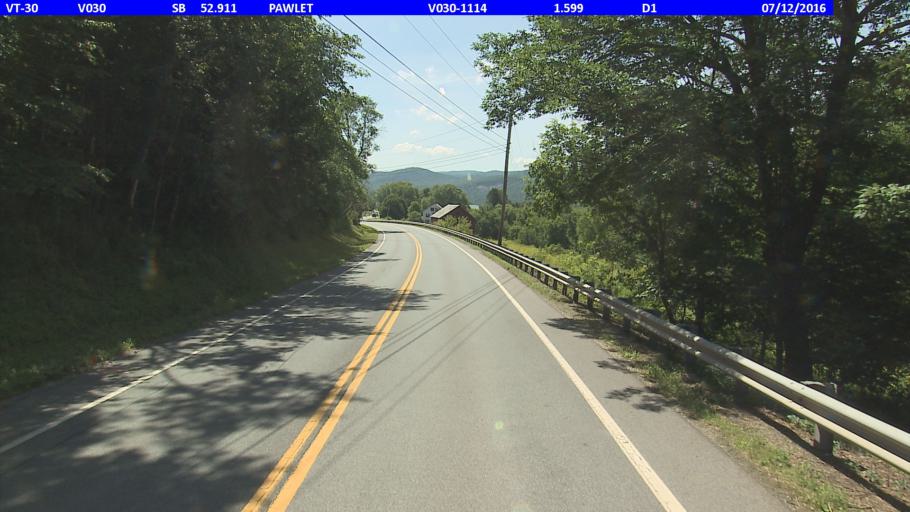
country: US
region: New York
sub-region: Washington County
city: Granville
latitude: 43.3331
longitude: -73.1762
